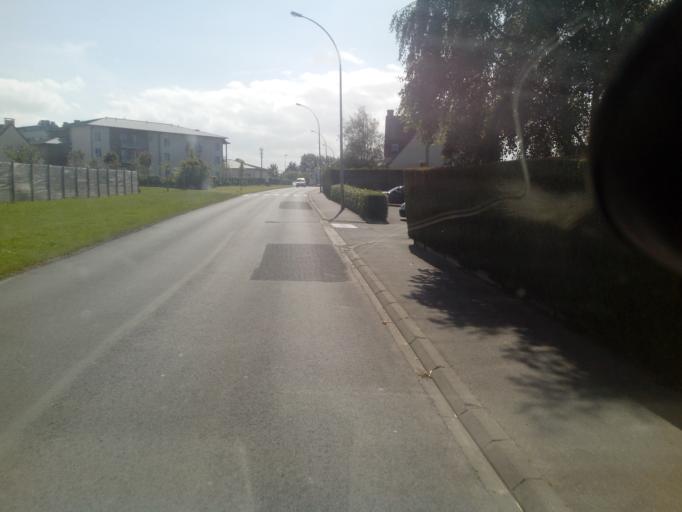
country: FR
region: Lower Normandy
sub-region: Departement du Calvados
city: Courseulles-sur-Mer
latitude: 49.3239
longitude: -0.4505
